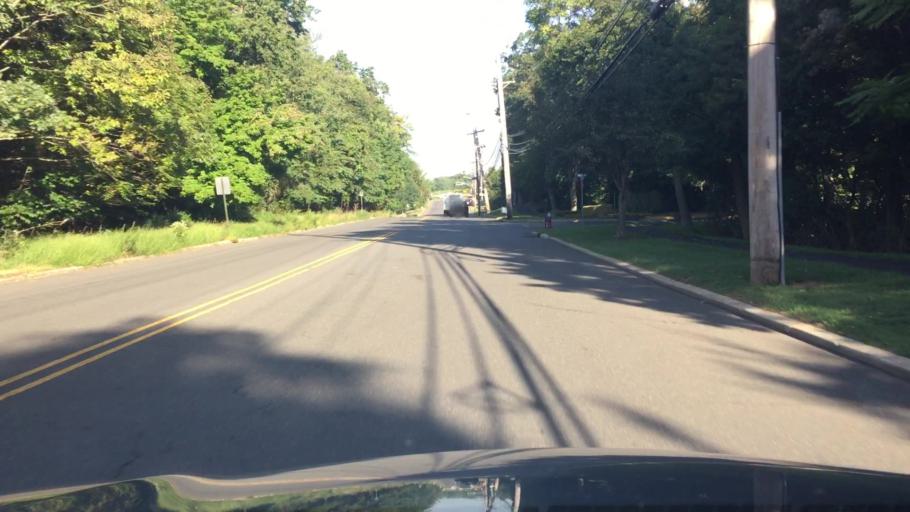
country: US
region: New Jersey
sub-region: Somerset County
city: Middlebush
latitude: 40.5193
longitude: -74.5194
